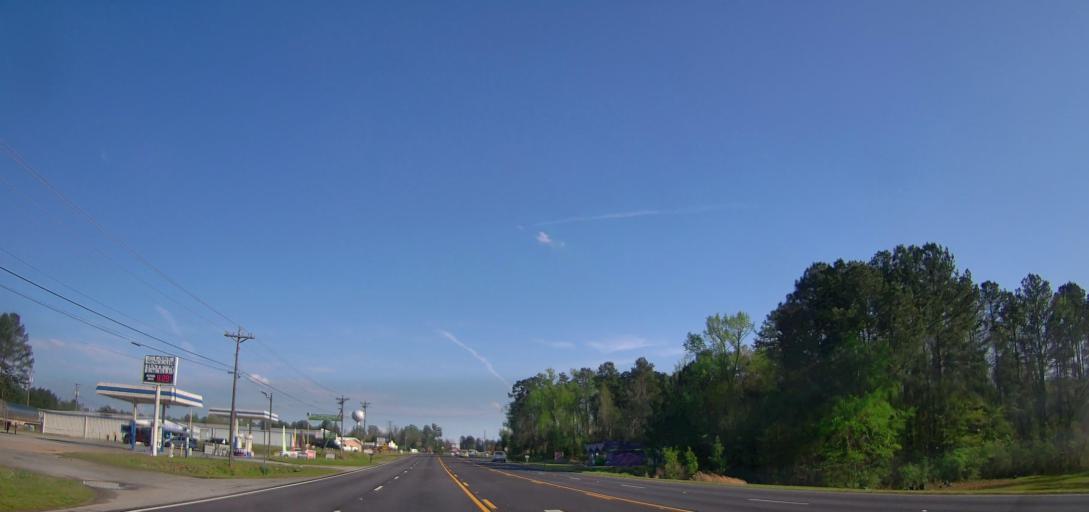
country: US
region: Georgia
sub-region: Baldwin County
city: Milledgeville
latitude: 33.1755
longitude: -83.2845
